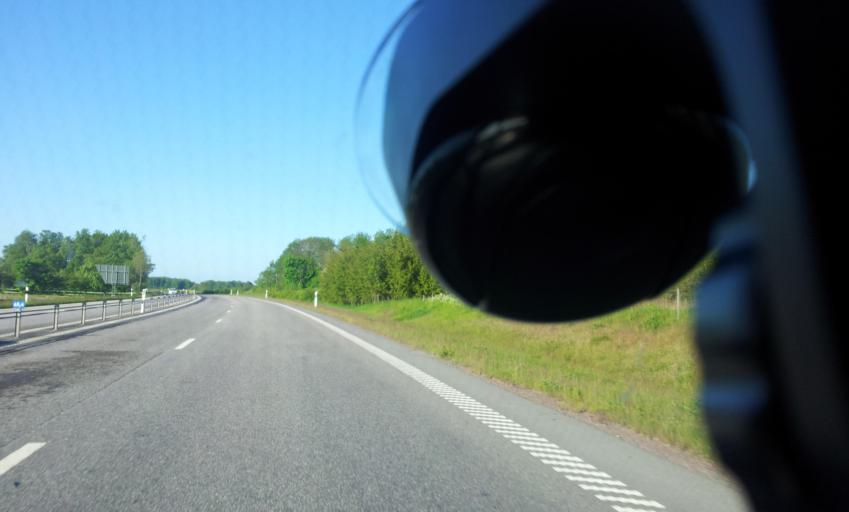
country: SE
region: Kalmar
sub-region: Kalmar Kommun
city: Lindsdal
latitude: 56.7912
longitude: 16.3479
